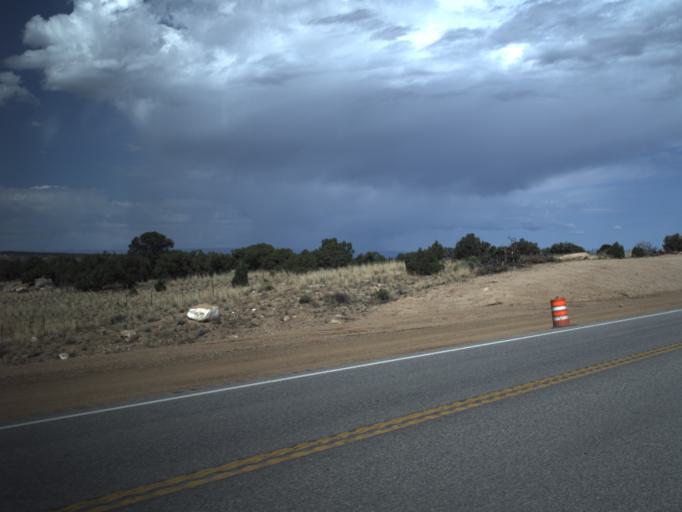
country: US
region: Utah
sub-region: Carbon County
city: East Carbon City
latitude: 39.4028
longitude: -110.4251
